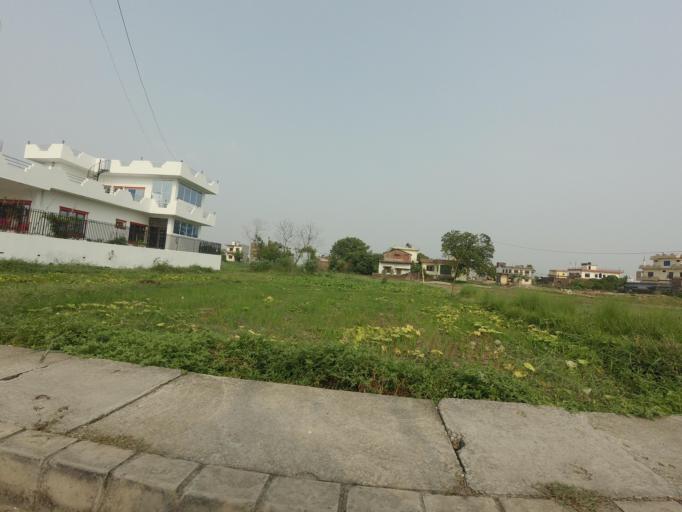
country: NP
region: Western Region
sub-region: Lumbini Zone
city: Bhairahawa
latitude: 27.5242
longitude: 83.4582
